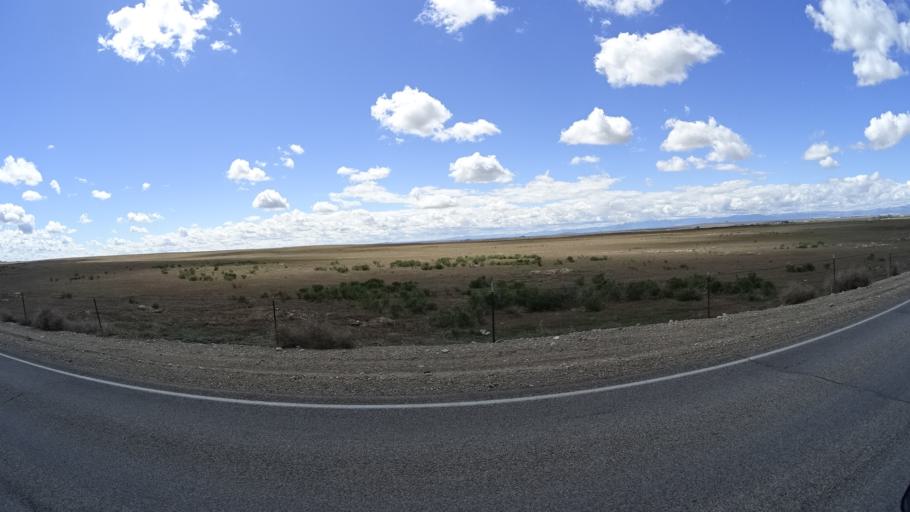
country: US
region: Idaho
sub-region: Ada County
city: Kuna
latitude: 43.4592
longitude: -116.2986
